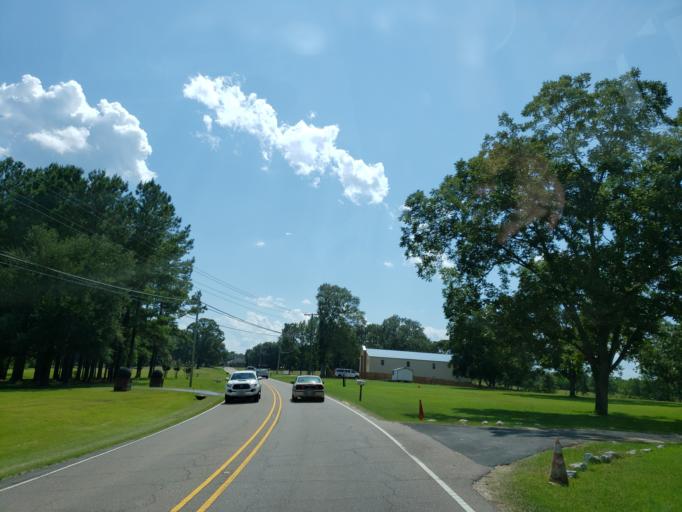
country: US
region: Mississippi
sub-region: Lamar County
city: West Hattiesburg
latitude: 31.2984
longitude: -89.3831
